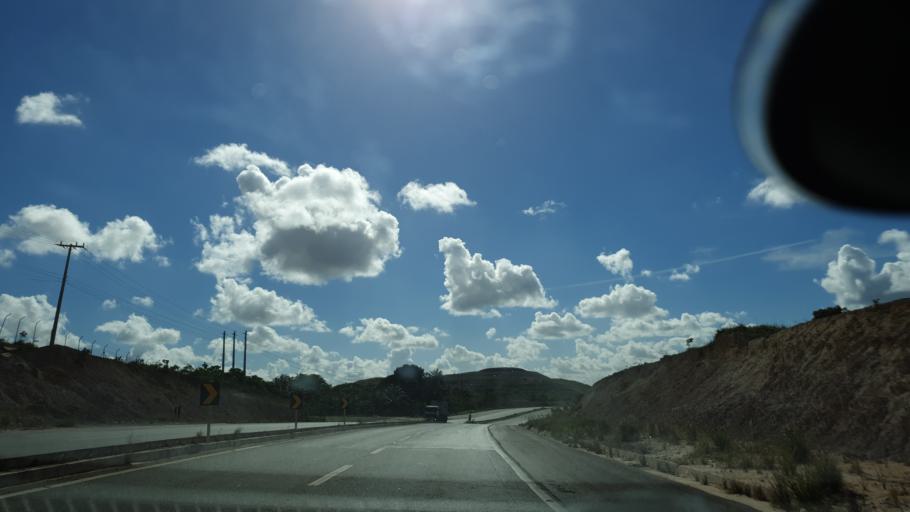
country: BR
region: Bahia
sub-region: Camacari
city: Camacari
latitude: -12.6849
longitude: -38.2516
